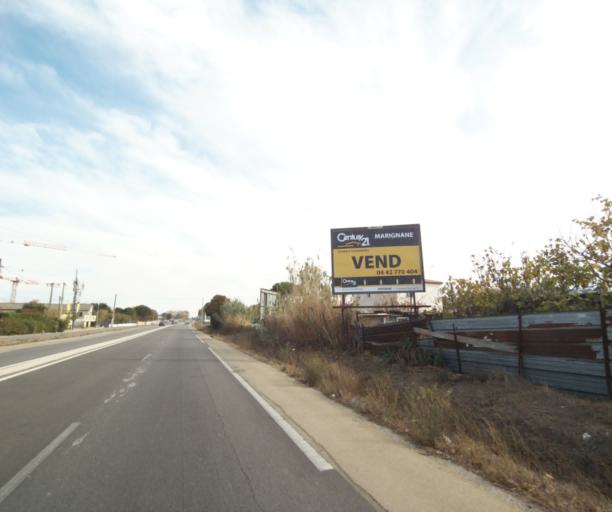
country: FR
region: Provence-Alpes-Cote d'Azur
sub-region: Departement des Bouches-du-Rhone
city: Gignac-la-Nerthe
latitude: 43.3962
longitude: 5.2417
